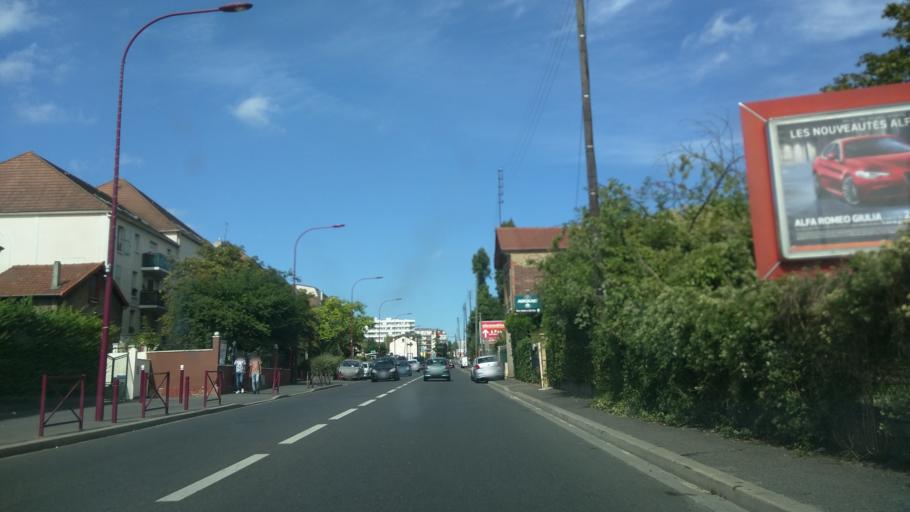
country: FR
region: Ile-de-France
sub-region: Departement du Val-d'Oise
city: Bezons
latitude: 48.9327
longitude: 2.2106
